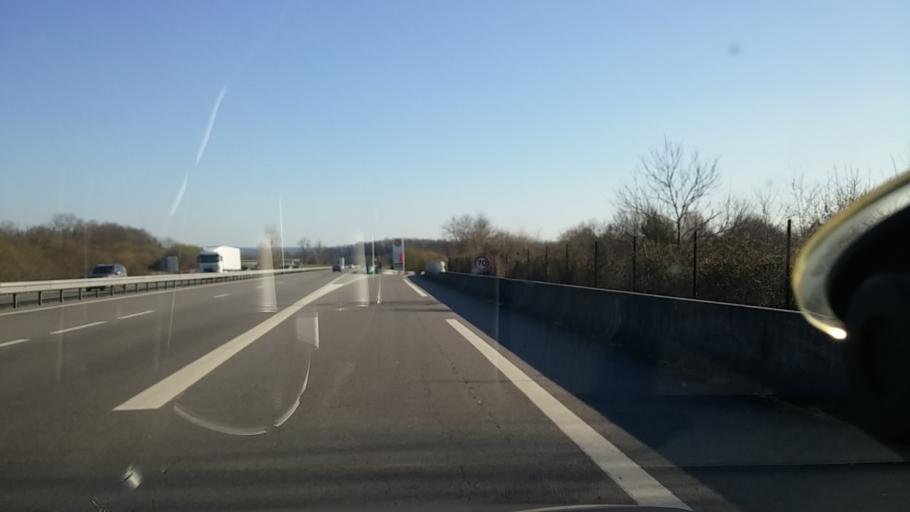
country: FR
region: Limousin
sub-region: Departement de la Haute-Vienne
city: Saint-Sulpice-les-Feuilles
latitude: 46.3176
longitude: 1.4177
